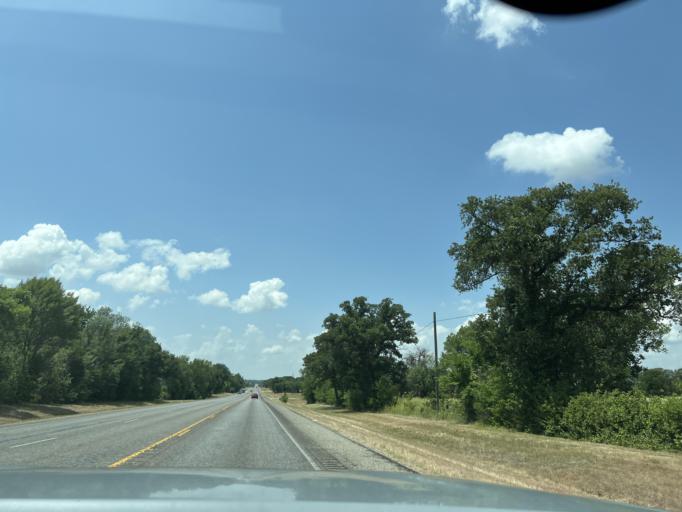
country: US
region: Texas
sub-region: Parker County
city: Springtown
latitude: 32.8871
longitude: -97.7352
